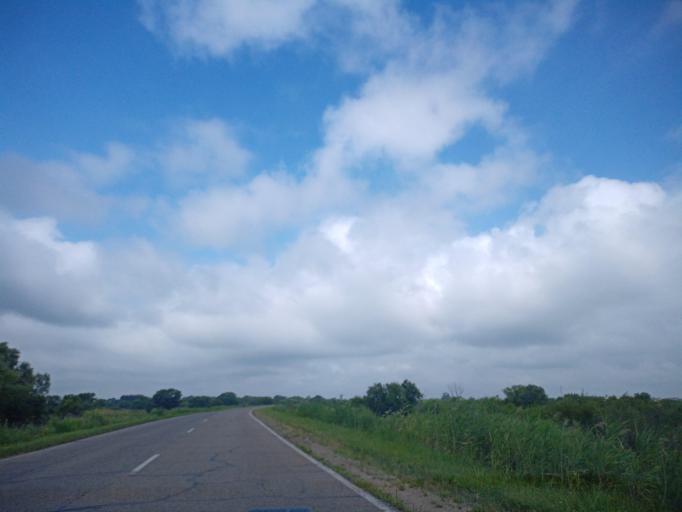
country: RU
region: Primorskiy
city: Dal'nerechensk
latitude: 45.9339
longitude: 133.8348
